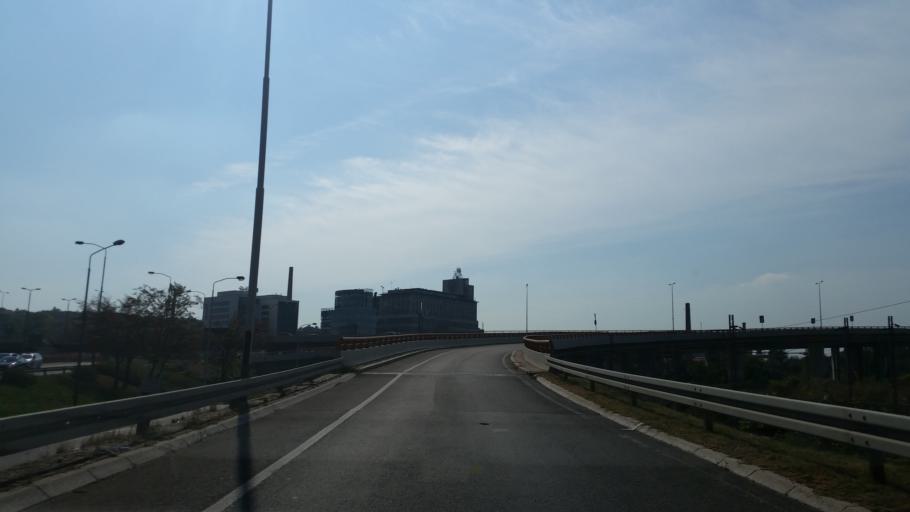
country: RS
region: Central Serbia
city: Belgrade
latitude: 44.8005
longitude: 20.4494
